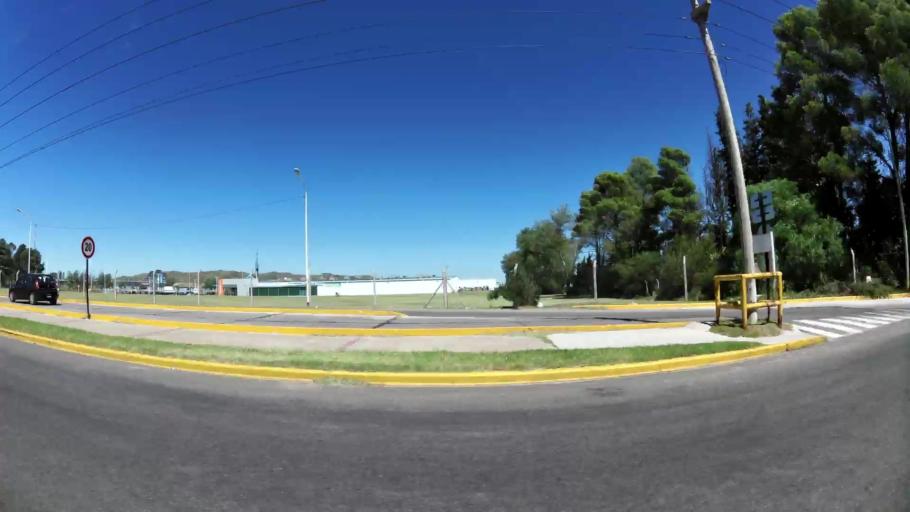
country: AR
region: San Luis
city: San Luis
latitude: -33.2943
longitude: -66.3038
